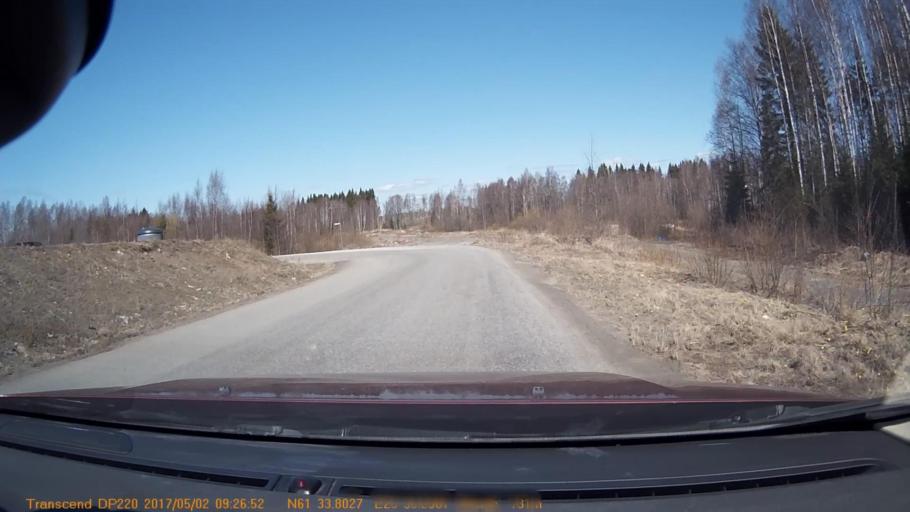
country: FI
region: Pirkanmaa
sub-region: Tampere
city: Yloejaervi
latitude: 61.5635
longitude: 23.5540
